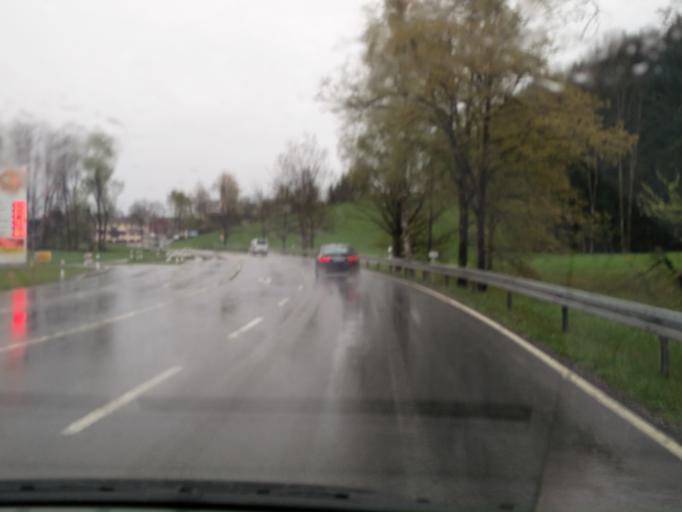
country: DE
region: Bavaria
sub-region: Upper Bavaria
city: Bernau am Chiemsee
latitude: 47.8136
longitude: 12.3661
